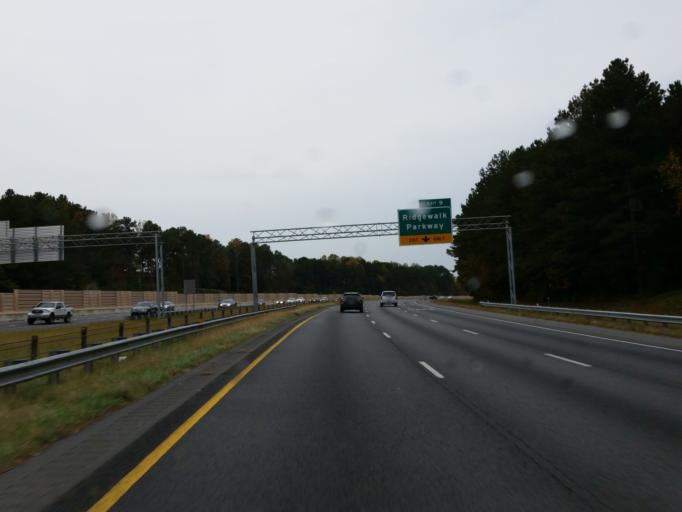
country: US
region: Georgia
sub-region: Cherokee County
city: Woodstock
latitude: 34.1134
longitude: -84.5337
